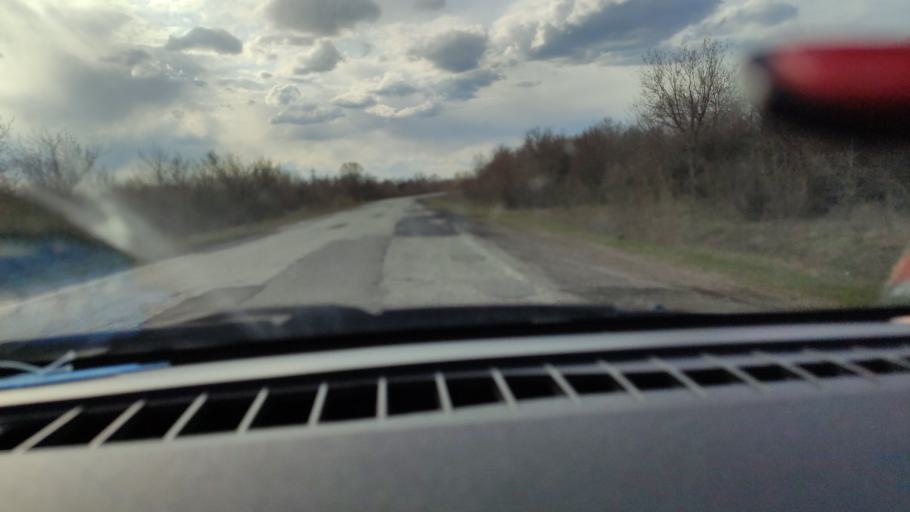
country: RU
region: Saratov
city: Krasnoarmeysk
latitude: 51.0731
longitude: 45.9828
